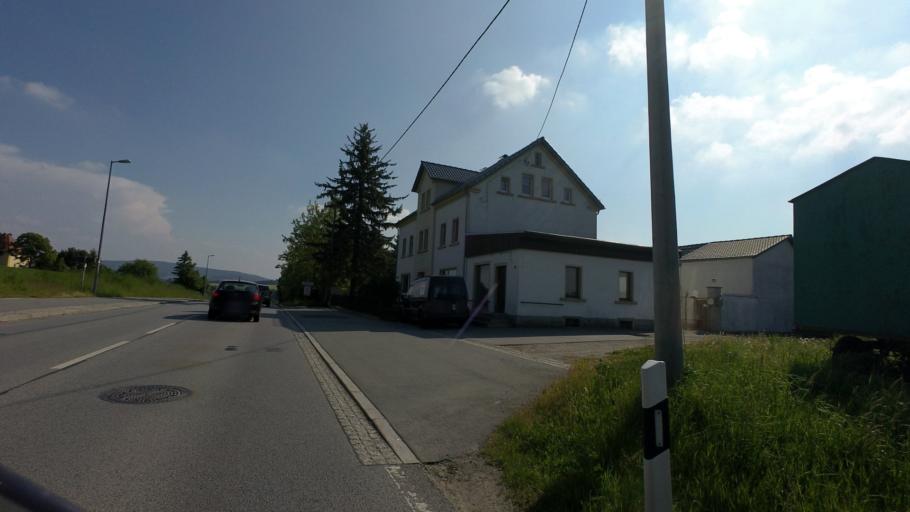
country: DE
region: Saxony
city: Grosspostwitz
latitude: 51.1277
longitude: 14.4410
